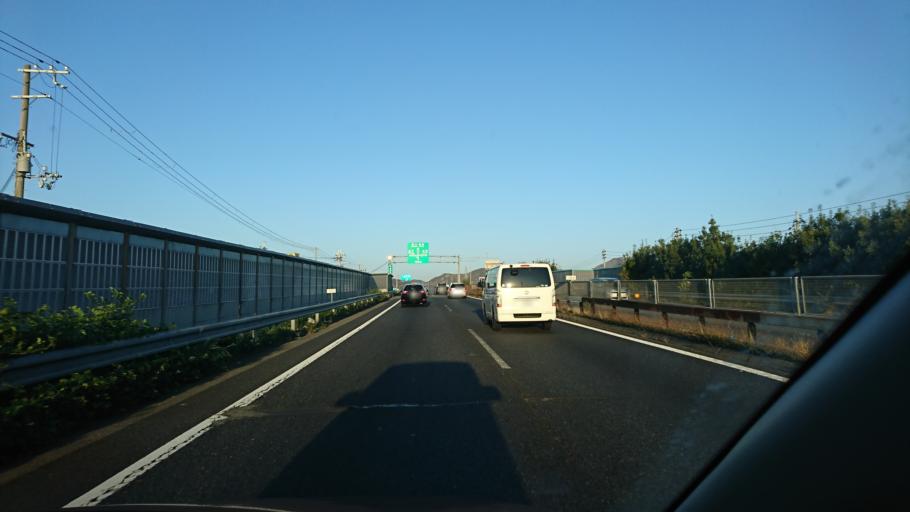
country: JP
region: Hyogo
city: Kakogawacho-honmachi
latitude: 34.7855
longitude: 134.8252
